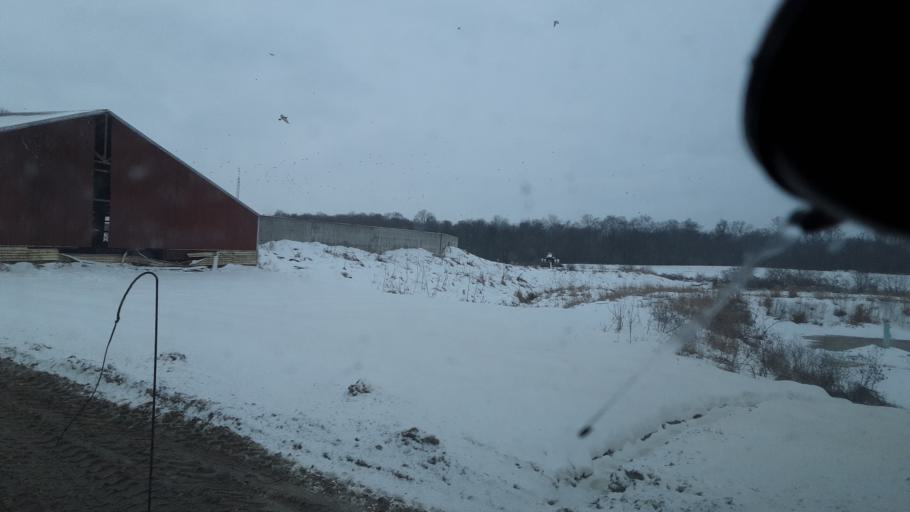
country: US
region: Ohio
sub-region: Licking County
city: Hebron
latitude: 39.9749
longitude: -82.4615
